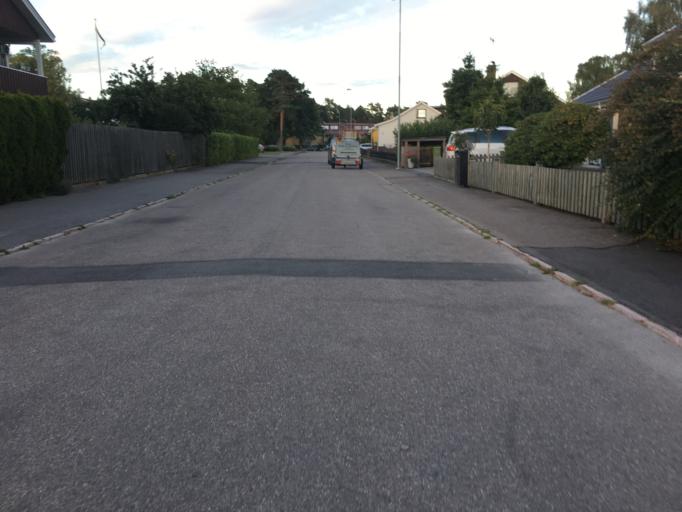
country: SE
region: Kalmar
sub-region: Kalmar Kommun
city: Kalmar
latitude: 56.6964
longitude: 16.3545
